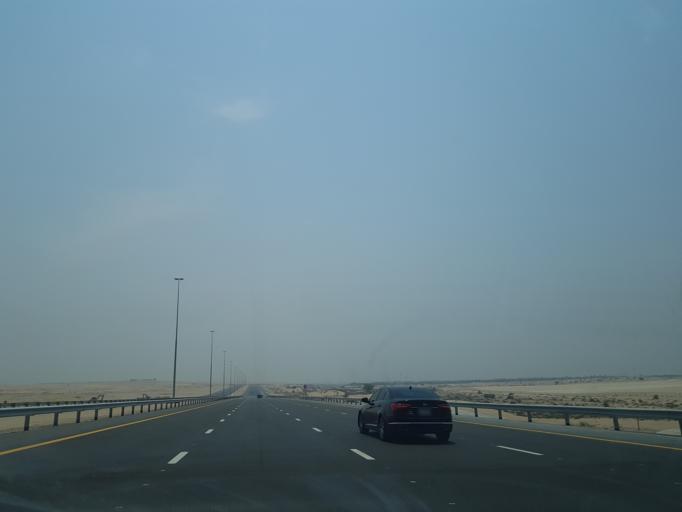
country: AE
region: Dubai
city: Dubai
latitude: 25.0190
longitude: 55.2299
